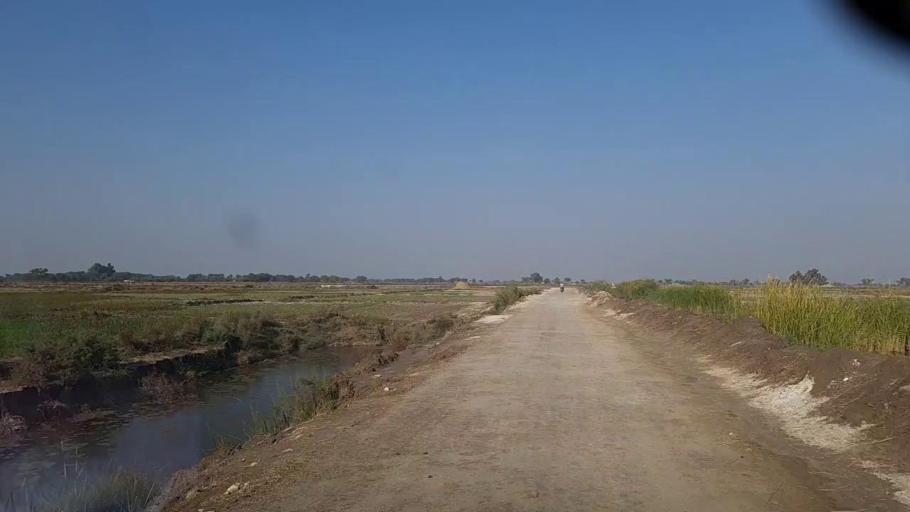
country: PK
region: Sindh
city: Jacobabad
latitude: 28.3094
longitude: 68.5616
